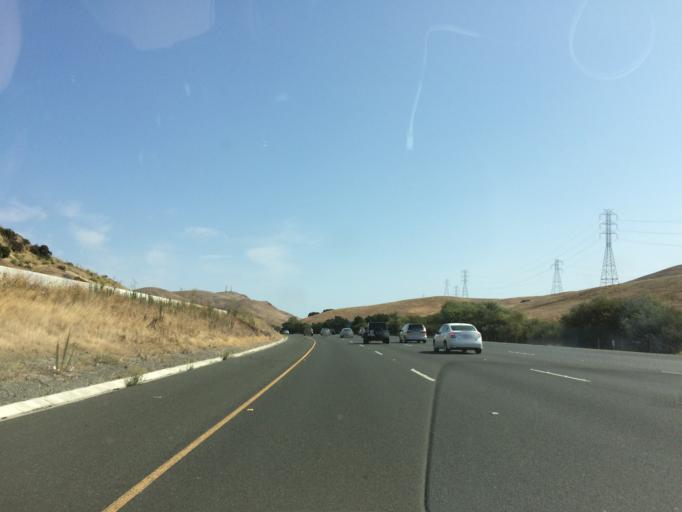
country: US
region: California
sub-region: Napa County
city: American Canyon
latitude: 38.1729
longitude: -122.1949
